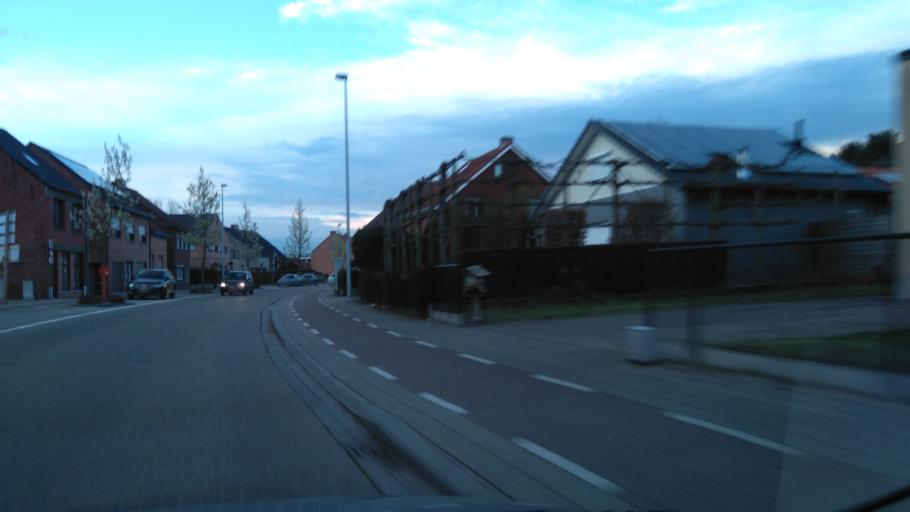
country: BE
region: Flanders
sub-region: Provincie Antwerpen
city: Oud-Turnhout
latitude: 51.3145
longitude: 4.9797
